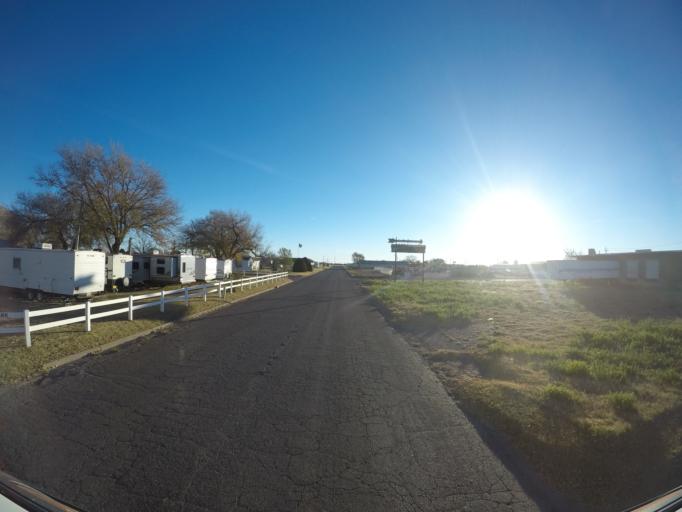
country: US
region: New Mexico
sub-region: Curry County
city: Clovis
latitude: 34.4007
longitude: -103.1833
